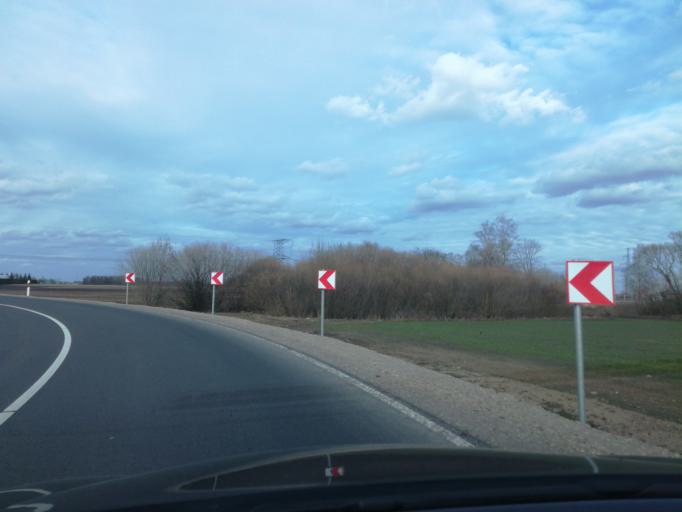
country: LT
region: Marijampoles apskritis
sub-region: Marijampole Municipality
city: Marijampole
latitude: 54.5940
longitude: 23.3969
